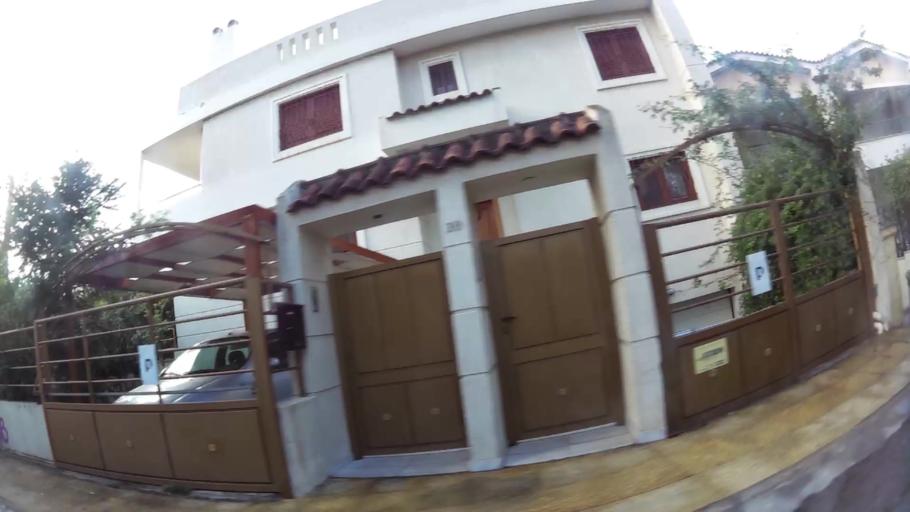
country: GR
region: Attica
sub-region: Nomarchia Athinas
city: Vrilissia
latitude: 38.0386
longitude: 23.8206
